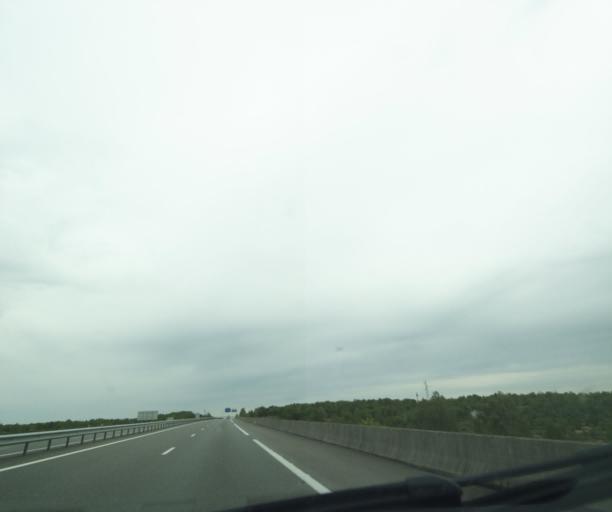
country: FR
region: Midi-Pyrenees
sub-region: Departement du Lot
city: Lalbenque
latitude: 44.3355
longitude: 1.5011
